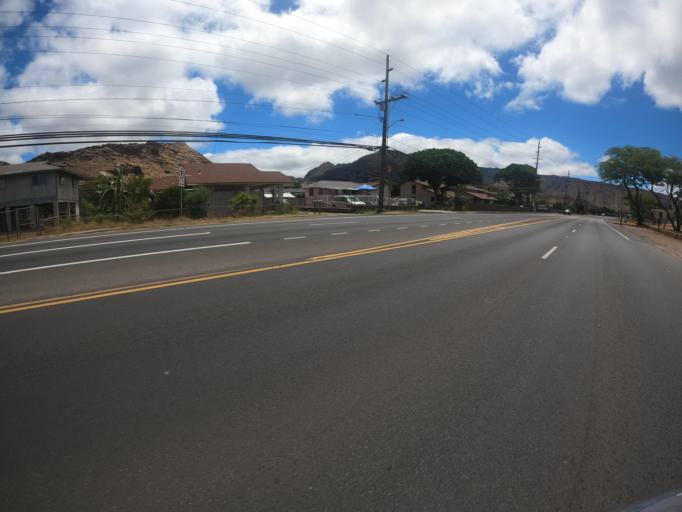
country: US
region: Hawaii
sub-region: Honolulu County
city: Nanakuli
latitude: 21.3955
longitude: -158.1629
